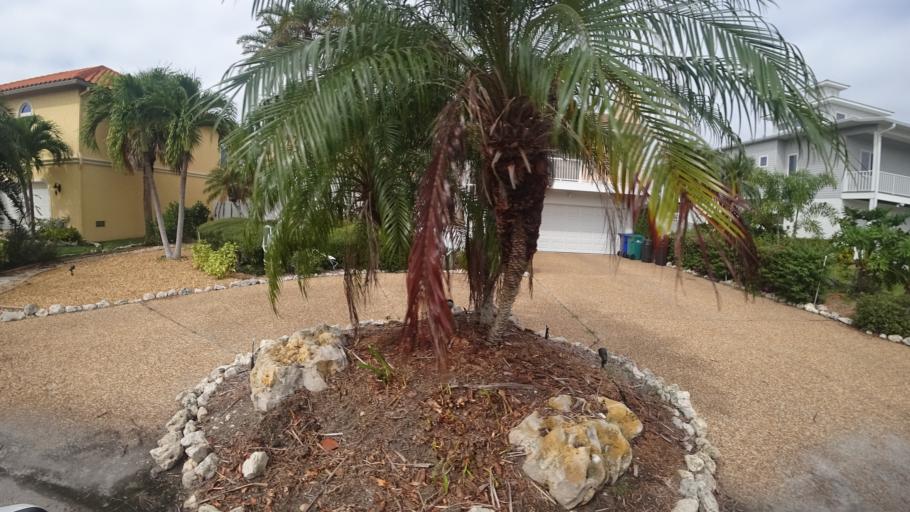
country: US
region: Florida
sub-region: Manatee County
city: Longboat Key
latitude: 27.4280
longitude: -82.6710
